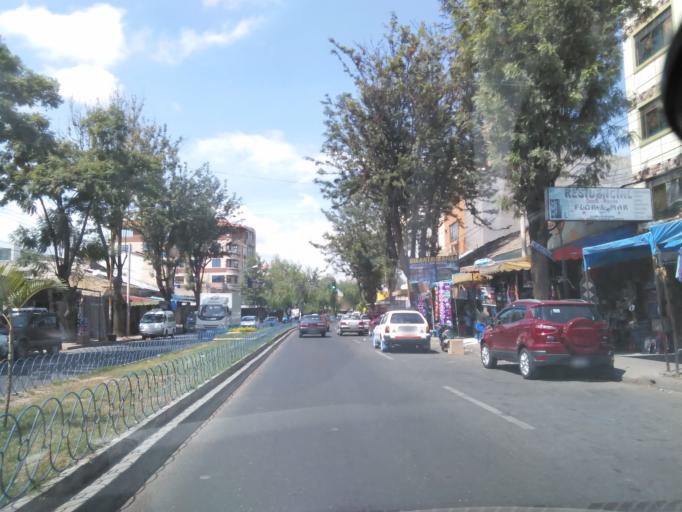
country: BO
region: Cochabamba
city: Cochabamba
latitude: -17.4024
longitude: -66.1630
